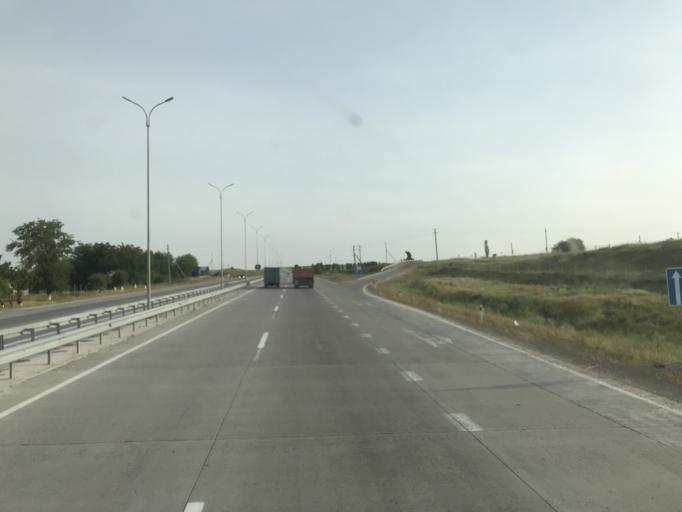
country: UZ
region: Toshkent
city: Qibray
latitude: 41.5644
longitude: 69.4085
